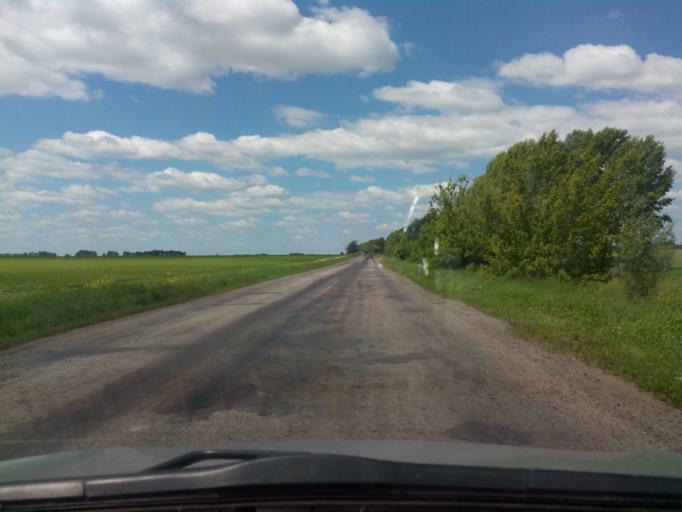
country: RU
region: Voronezj
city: Gribanovskiy
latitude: 51.6211
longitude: 41.9579
